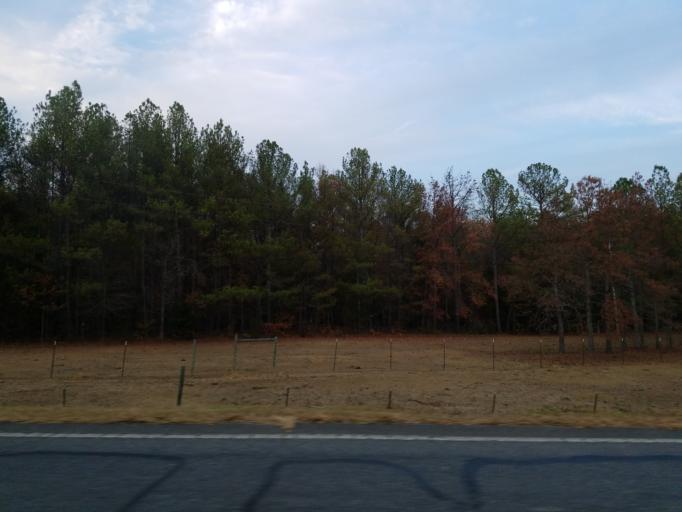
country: US
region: Georgia
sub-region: Murray County
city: Chatsworth
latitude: 34.6022
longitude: -84.7914
